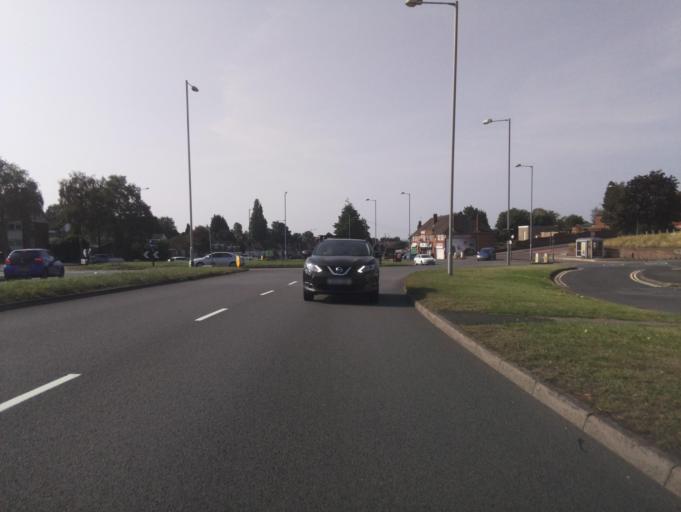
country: GB
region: England
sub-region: Walsall
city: Streetly
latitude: 52.5565
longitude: -1.8982
